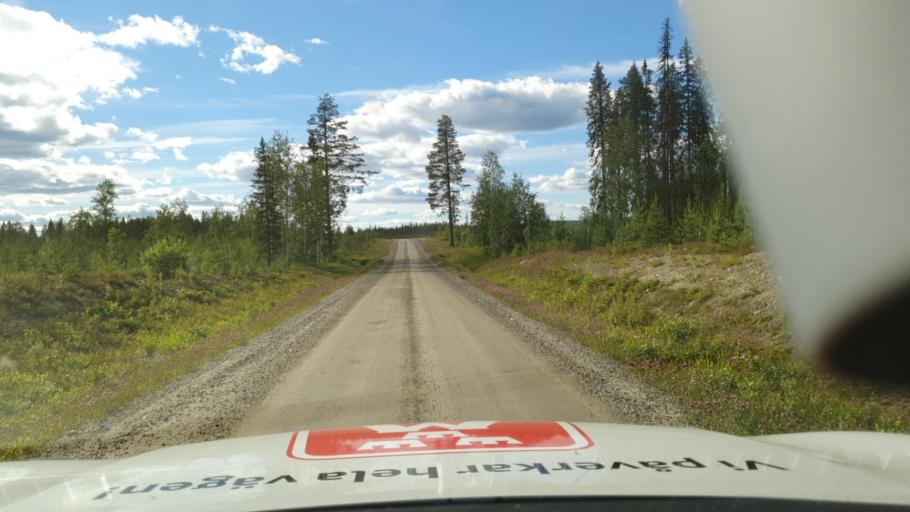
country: SE
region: Vaesterbotten
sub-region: Lycksele Kommun
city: Lycksele
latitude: 64.3904
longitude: 18.5963
